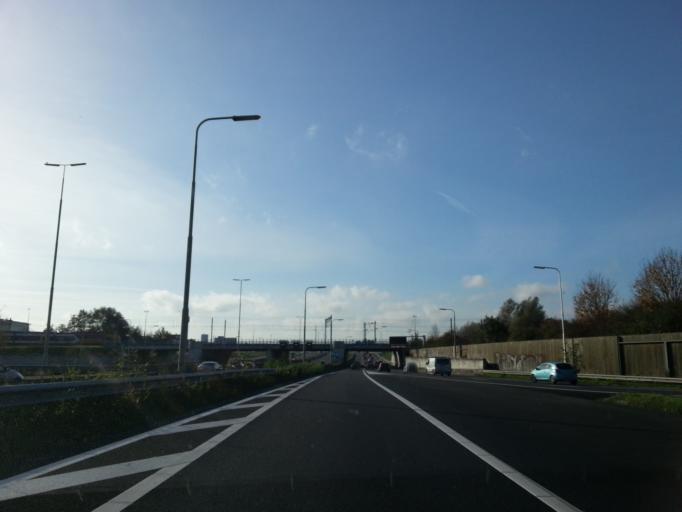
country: NL
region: South Holland
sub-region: Gemeente Leidschendam-Voorburg
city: Voorburg
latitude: 52.0728
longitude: 4.3925
